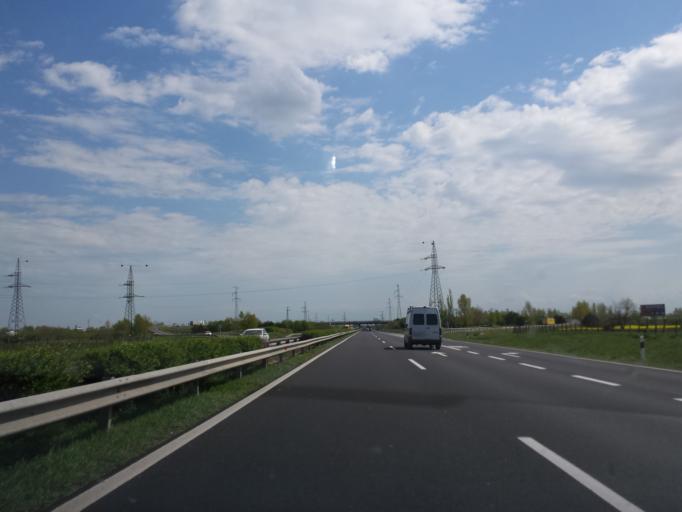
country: HU
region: Gyor-Moson-Sopron
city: Mosonmagyarovar
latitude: 47.8552
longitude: 17.2438
